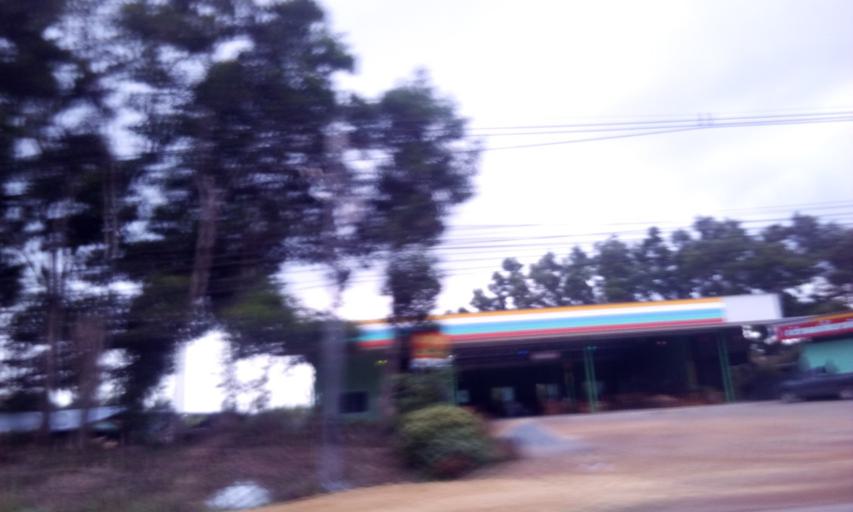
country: TH
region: Chanthaburi
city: Khlung
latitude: 12.4539
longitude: 102.2800
